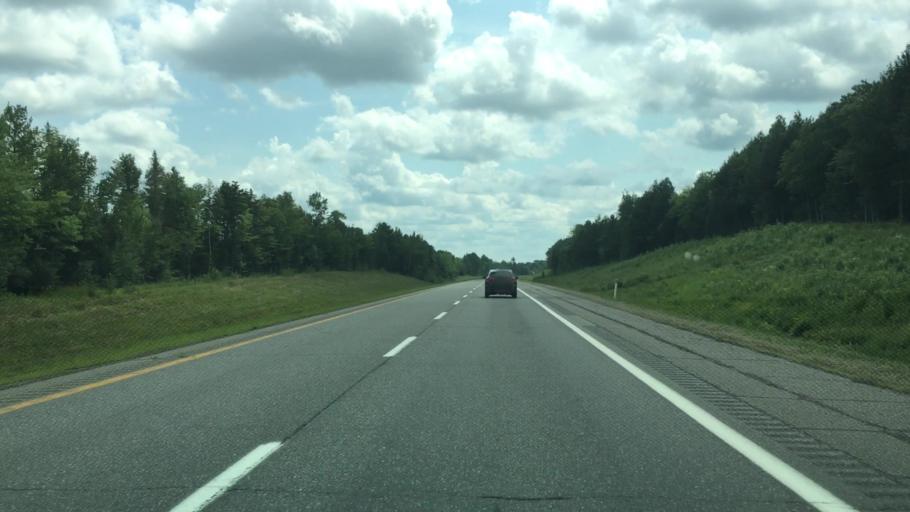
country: US
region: Maine
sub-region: Penobscot County
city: Howland
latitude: 45.2960
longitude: -68.6641
